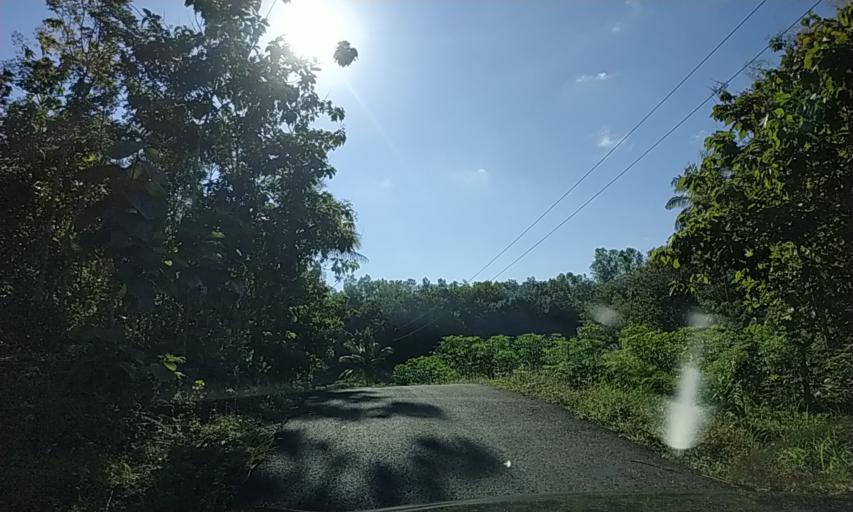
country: ID
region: East Java
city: Krajan
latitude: -8.1284
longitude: 110.9031
